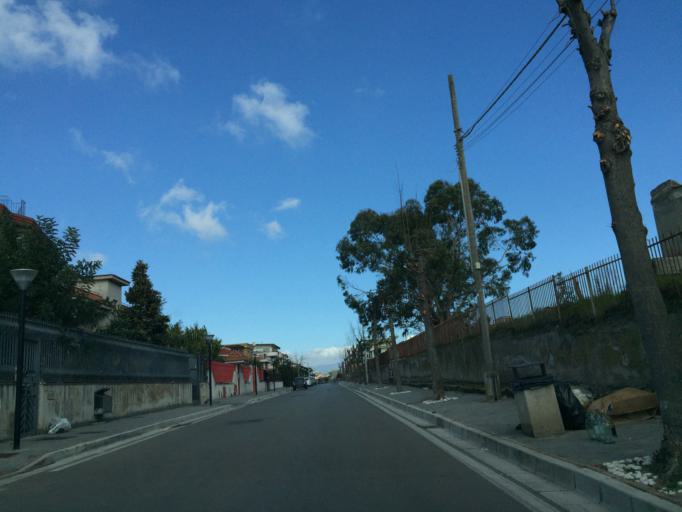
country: IT
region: Campania
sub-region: Provincia di Napoli
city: Pollena Trocchia
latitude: 40.8505
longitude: 14.3779
